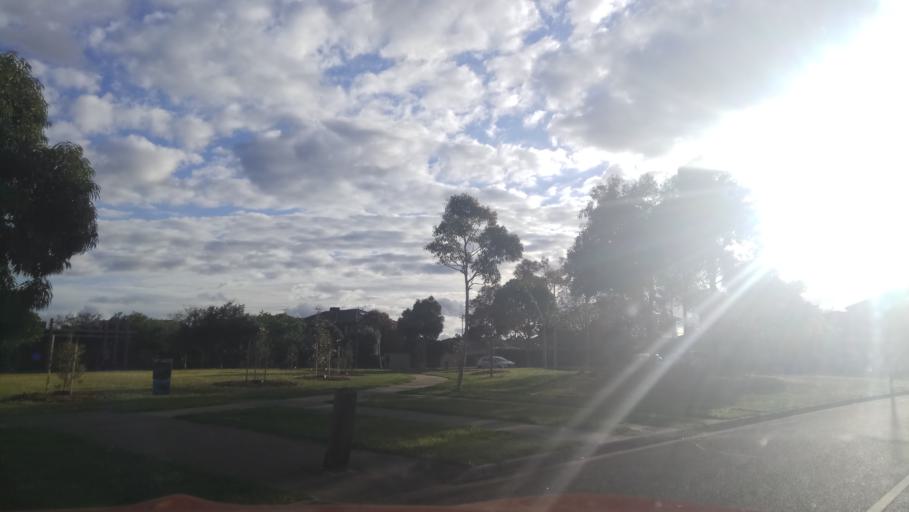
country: AU
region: Victoria
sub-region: Wyndham
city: Point Cook
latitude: -37.9020
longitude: 144.7492
